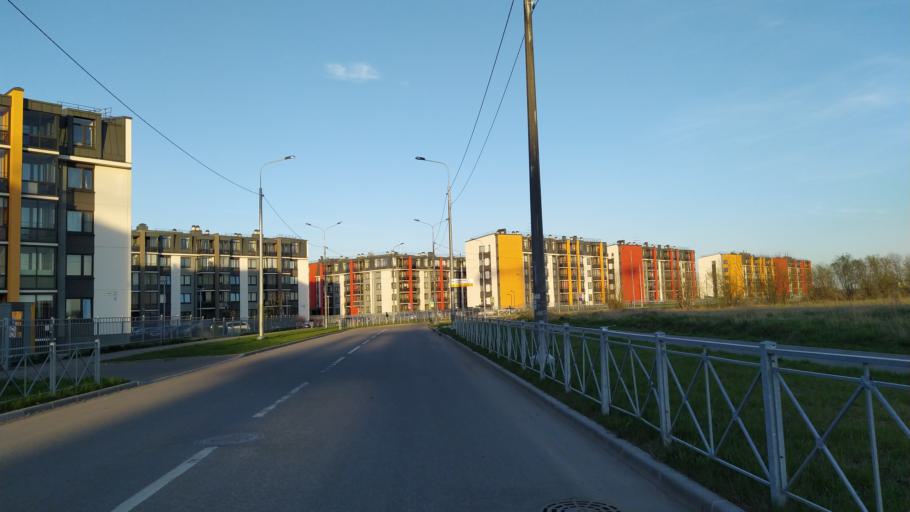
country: RU
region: St.-Petersburg
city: Pushkin
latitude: 59.6990
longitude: 30.4030
